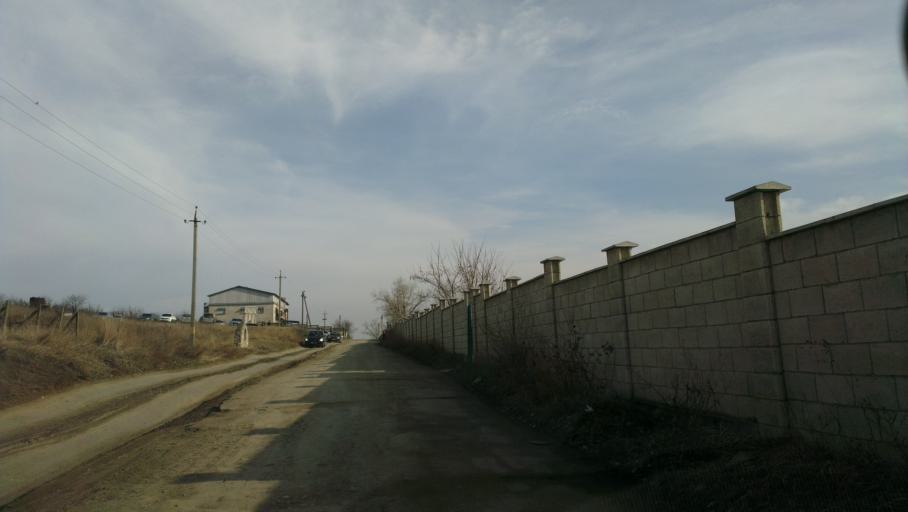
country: MD
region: Laloveni
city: Ialoveni
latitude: 46.9137
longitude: 28.7006
